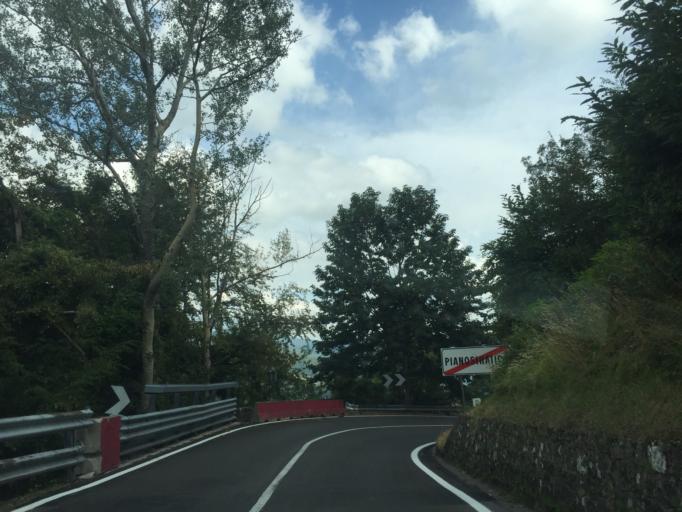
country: IT
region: Tuscany
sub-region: Provincia di Pistoia
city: Cutigliano
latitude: 44.1193
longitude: 10.7298
